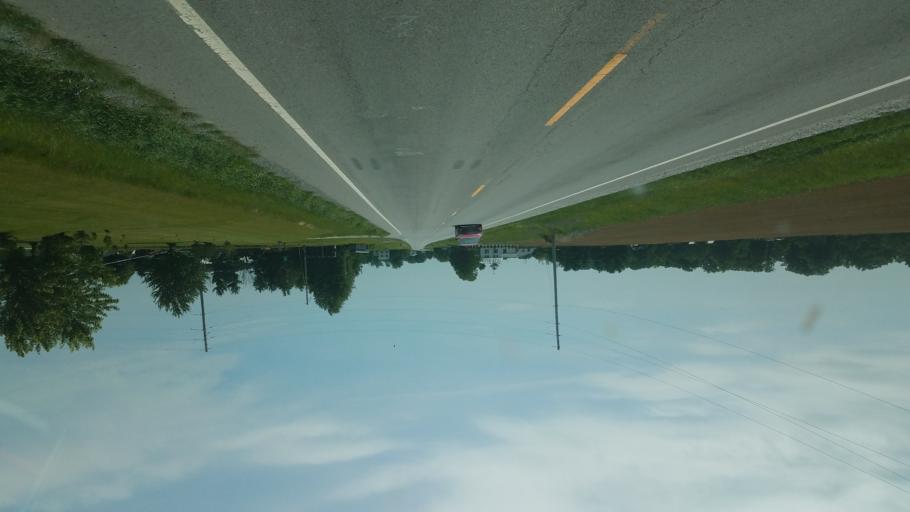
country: US
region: Ohio
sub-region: Wyandot County
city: Carey
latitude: 40.9026
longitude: -83.3344
